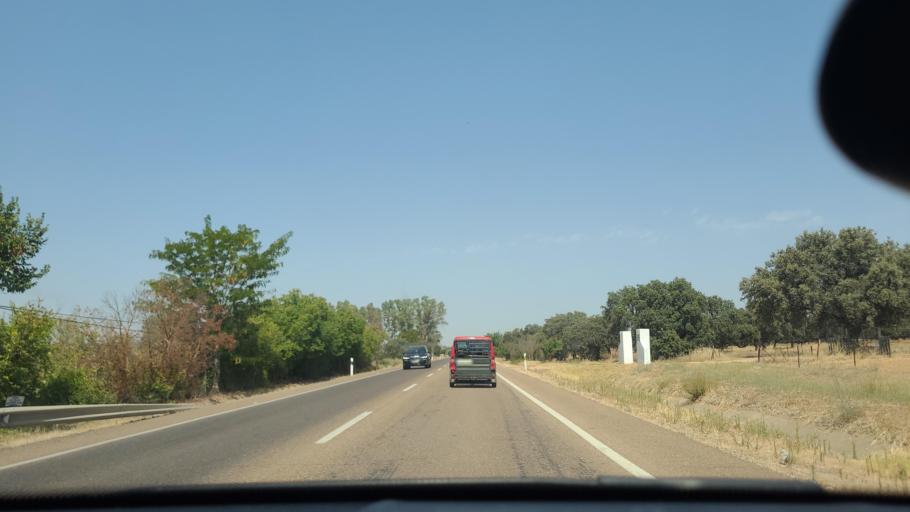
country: ES
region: Extremadura
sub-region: Provincia de Badajoz
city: Badajoz
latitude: 38.8346
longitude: -6.9223
